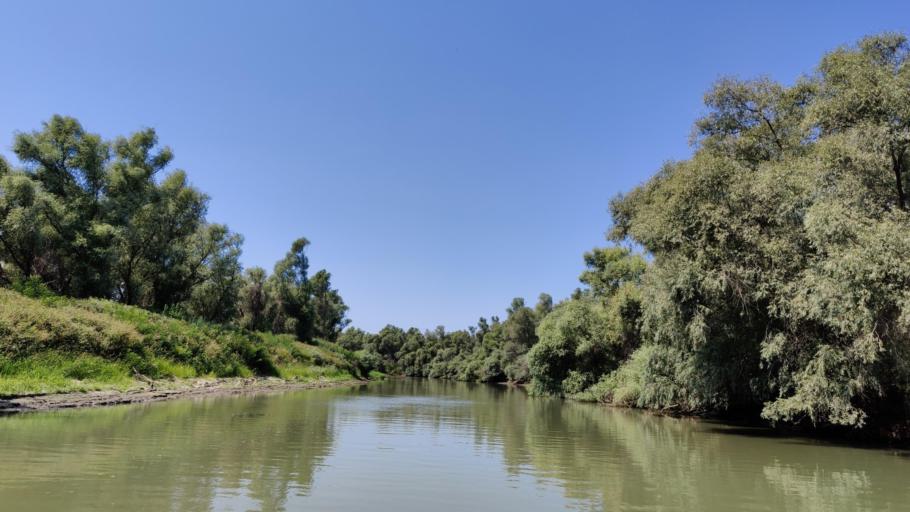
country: RO
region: Tulcea
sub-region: Comuna Pardina
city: Pardina
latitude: 45.2558
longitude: 28.9601
